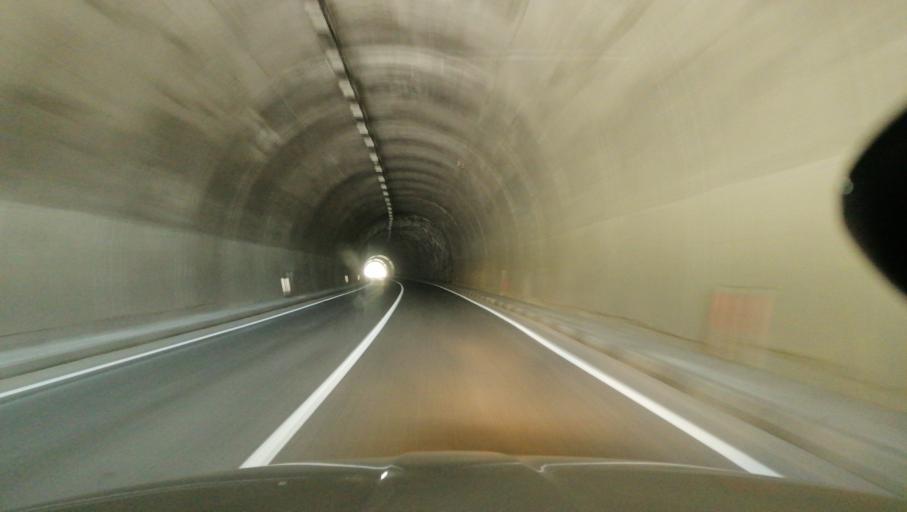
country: BA
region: Republika Srpska
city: Visegrad
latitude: 43.7508
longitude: 19.2510
